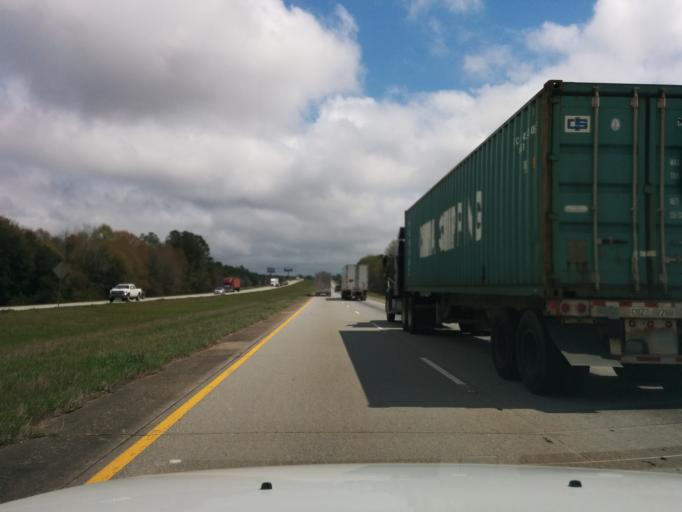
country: US
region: Georgia
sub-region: Emanuel County
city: Swainsboro
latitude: 32.4081
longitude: -82.3334
